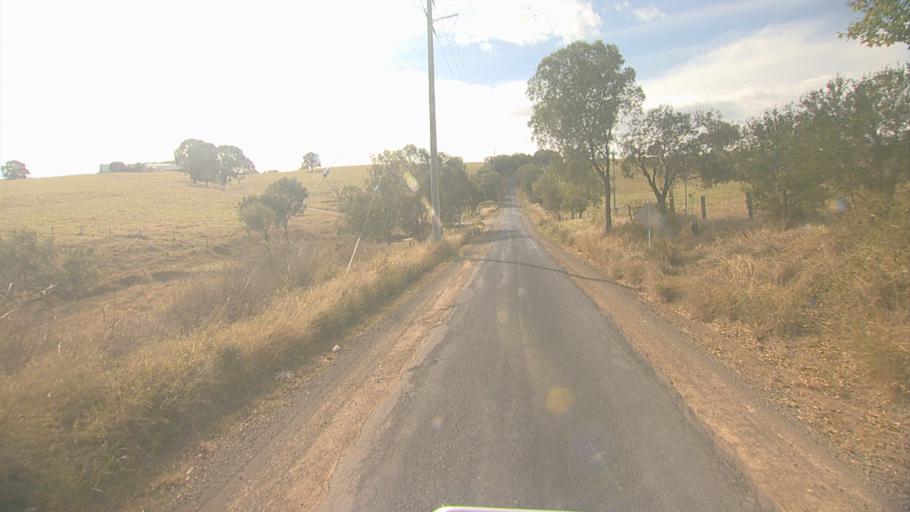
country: AU
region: Queensland
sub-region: Logan
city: Cedar Vale
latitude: -27.9090
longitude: 153.0134
